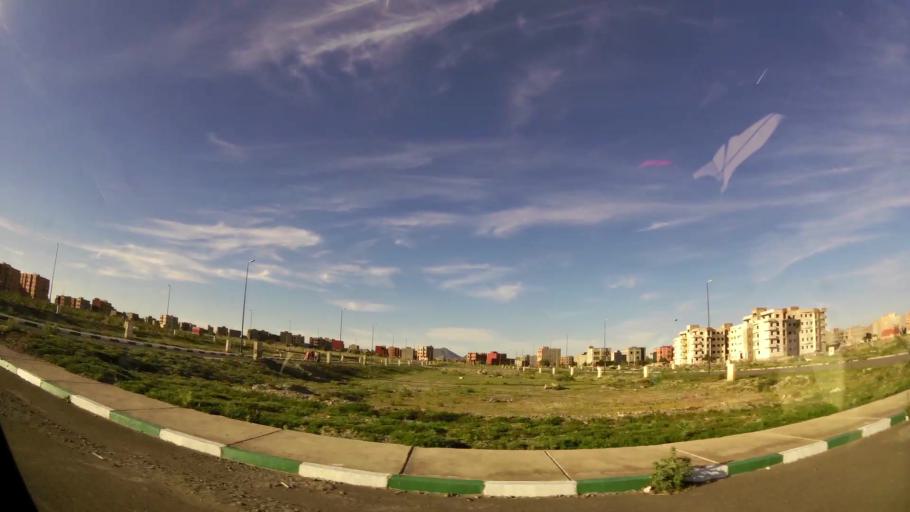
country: MA
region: Marrakech-Tensift-Al Haouz
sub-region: Marrakech
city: Marrakesh
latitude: 31.7631
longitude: -8.1060
